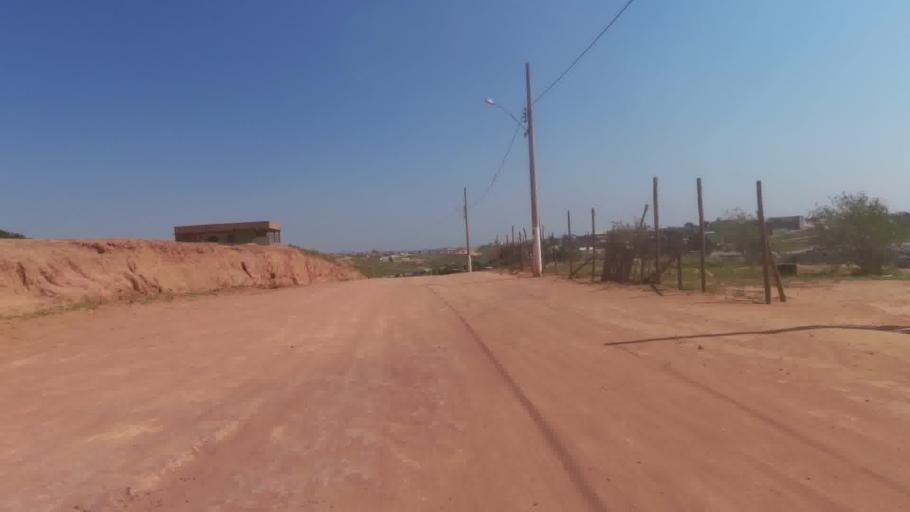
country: BR
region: Espirito Santo
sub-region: Itapemirim
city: Itapemirim
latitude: -21.0175
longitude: -40.8248
